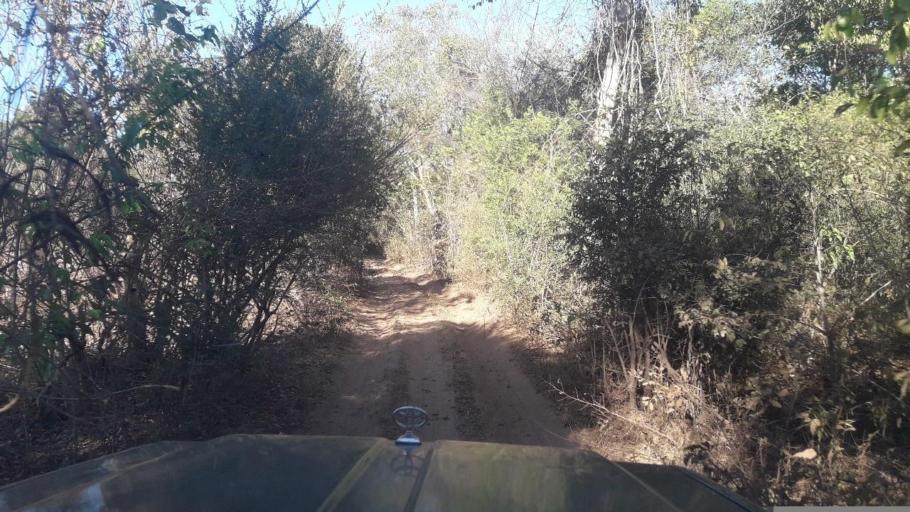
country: MG
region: Boeny
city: Sitampiky
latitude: -16.4269
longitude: 45.6248
